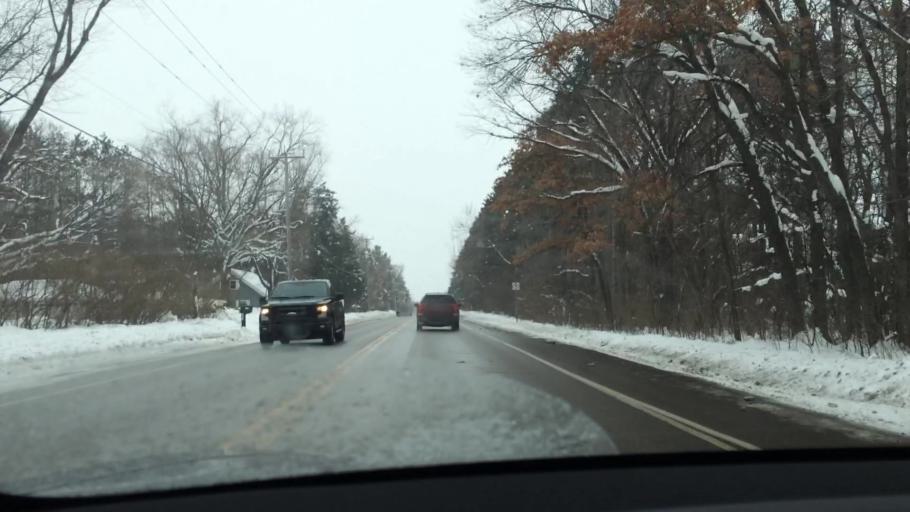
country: US
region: Minnesota
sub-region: Ramsey County
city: Shoreview
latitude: 45.0970
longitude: -93.1272
